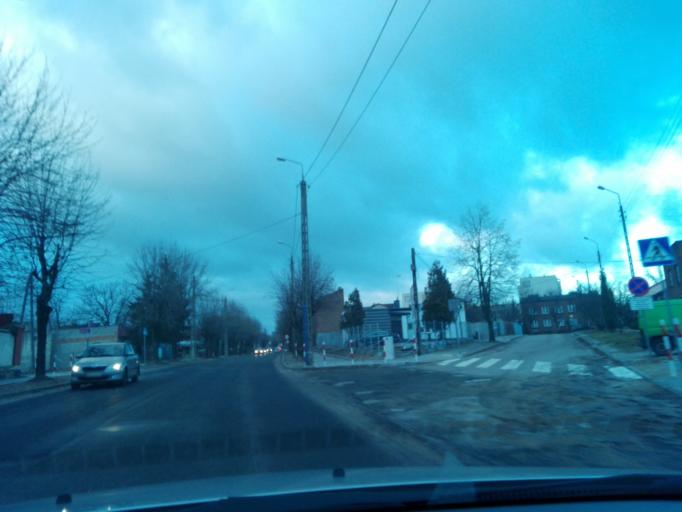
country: PL
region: Lodz Voivodeship
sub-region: Powiat kutnowski
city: Kutno
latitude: 52.2370
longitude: 19.3529
